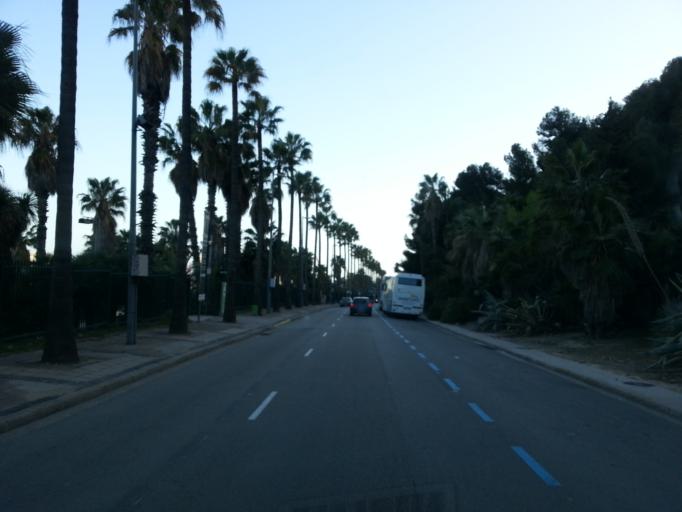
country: ES
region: Catalonia
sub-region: Provincia de Barcelona
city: Ciutat Vella
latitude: 41.3679
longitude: 2.1710
